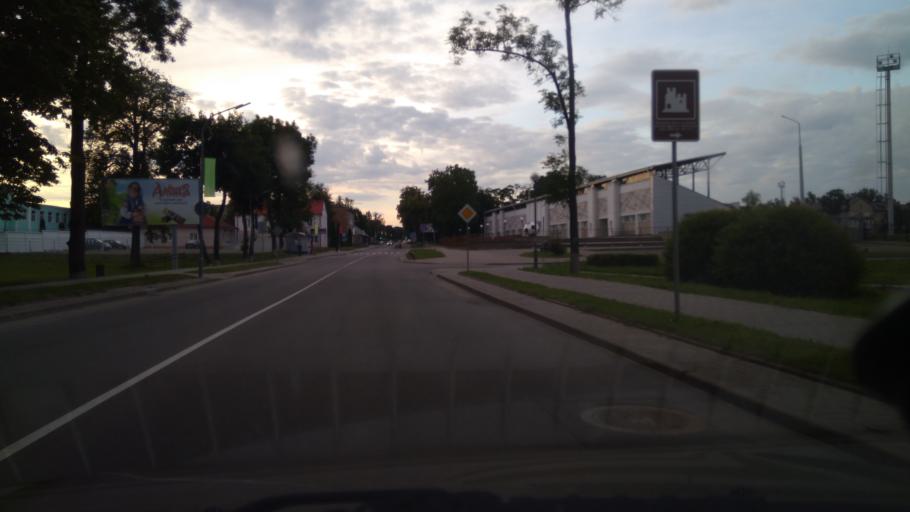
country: BY
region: Grodnenskaya
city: Shchuchin
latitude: 53.6090
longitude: 24.7386
